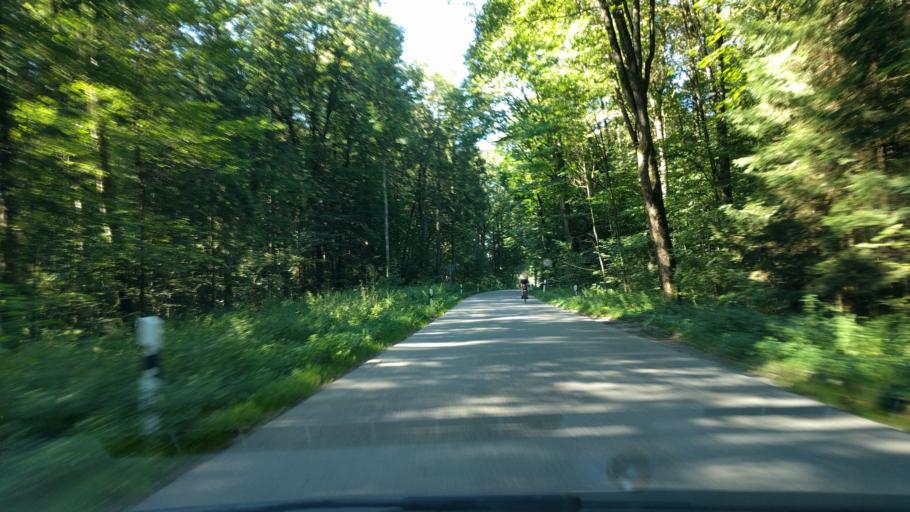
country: DE
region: Bavaria
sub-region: Upper Bavaria
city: Grunwald
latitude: 48.0358
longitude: 11.5503
